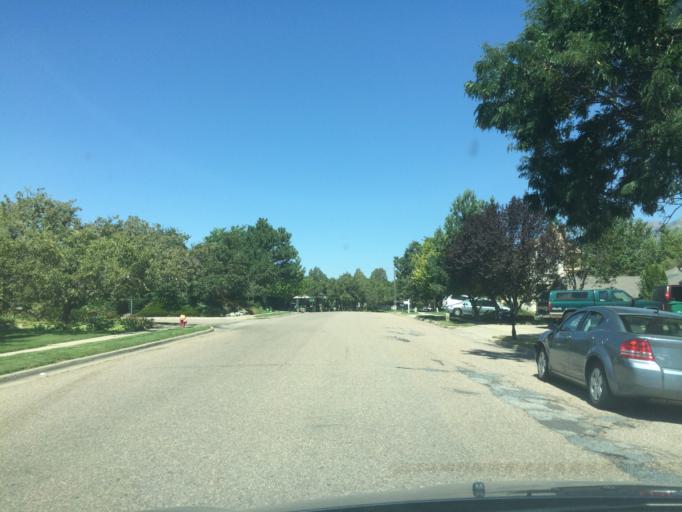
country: US
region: Utah
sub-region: Davis County
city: South Weber
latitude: 41.1081
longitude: -111.9190
